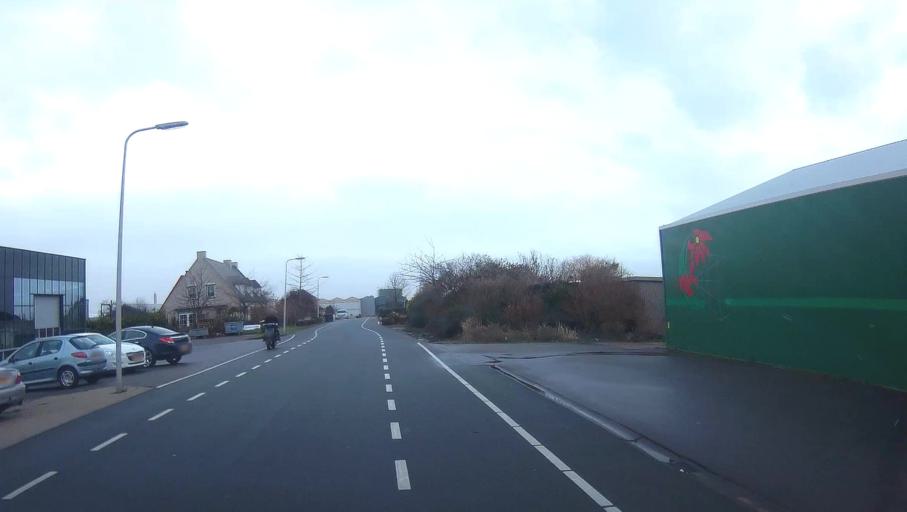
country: NL
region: South Holland
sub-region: Gemeente Westland
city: Poeldijk
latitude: 52.0283
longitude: 4.2031
